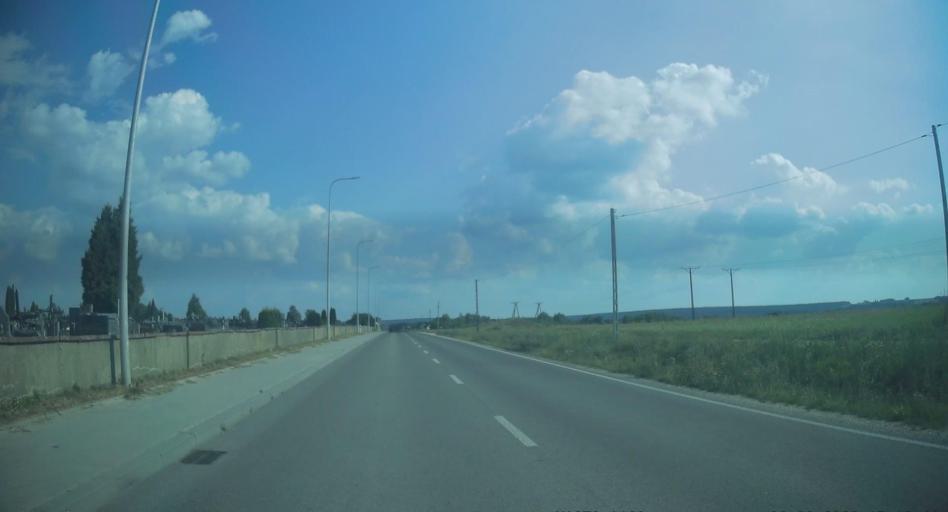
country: PL
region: Swietokrzyskie
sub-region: Powiat konecki
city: Radoszyce
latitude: 51.0689
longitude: 20.2697
